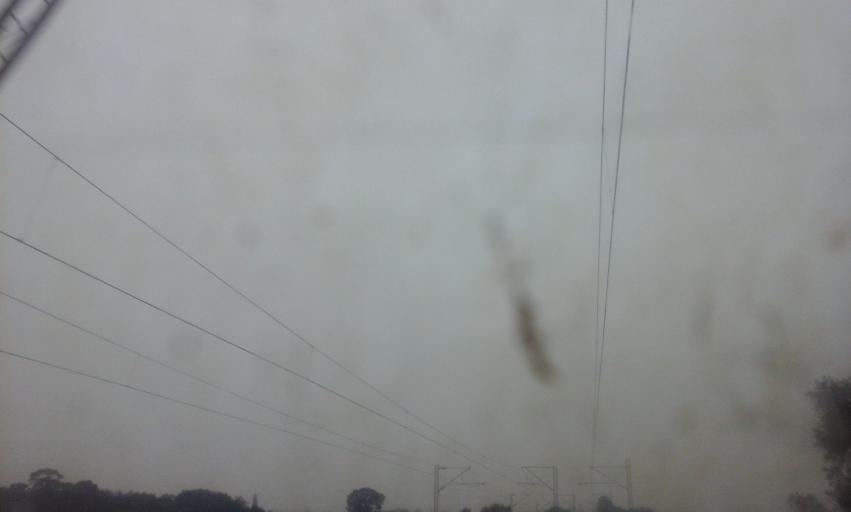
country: RS
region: Central Serbia
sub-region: Pomoravski Okrug
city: Paracin
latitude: 43.8805
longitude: 21.3874
